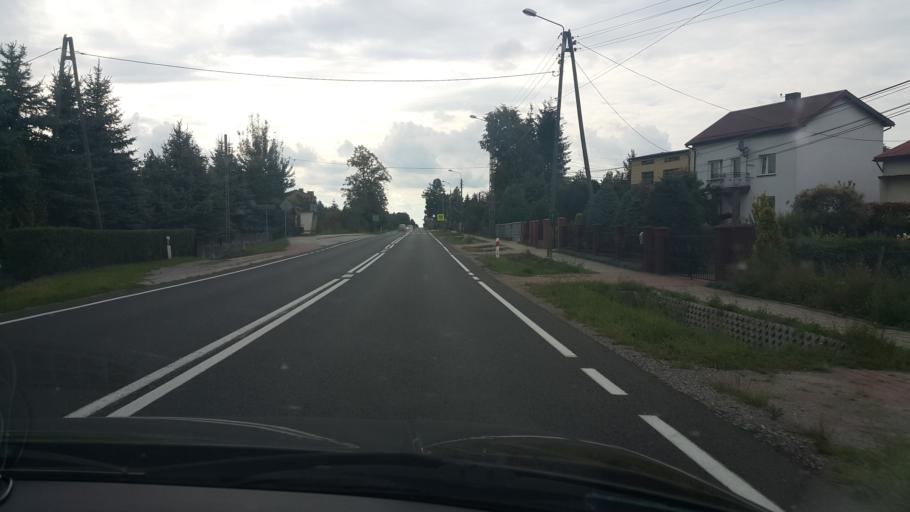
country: PL
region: Swietokrzyskie
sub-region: Powiat skarzyski
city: Blizyn
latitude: 51.1000
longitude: 20.7930
